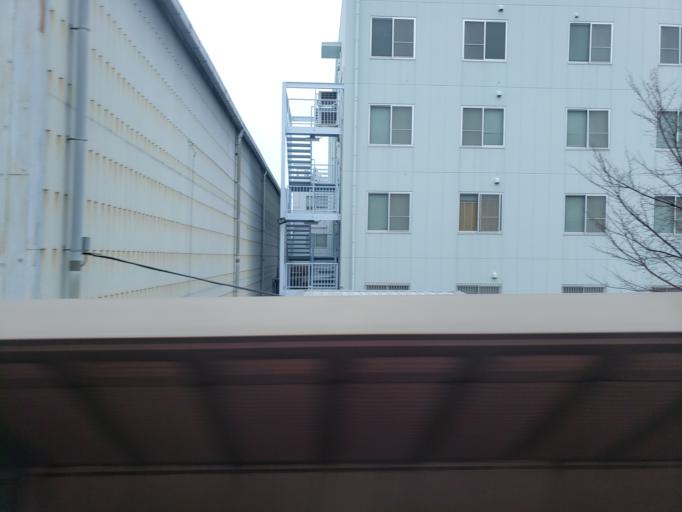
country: JP
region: Hyogo
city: Amagasaki
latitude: 34.7174
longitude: 135.4228
